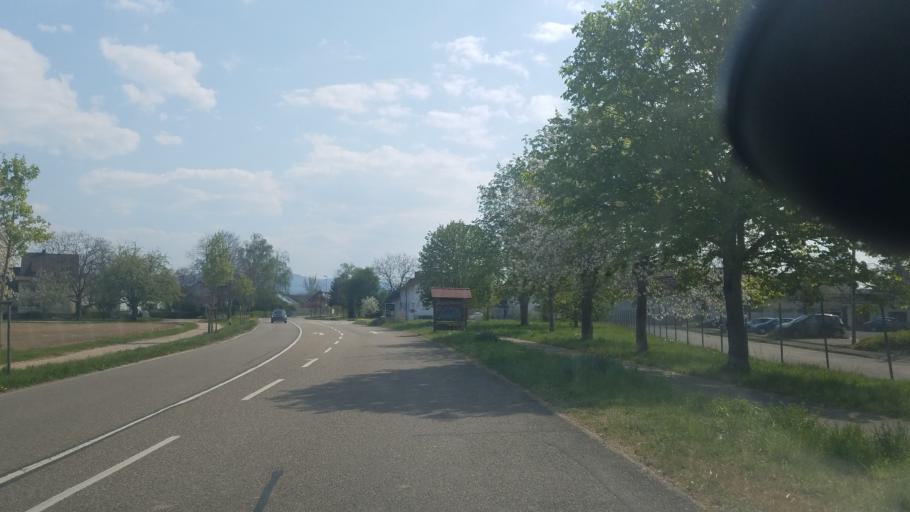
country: DE
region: Baden-Wuerttemberg
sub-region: Freiburg Region
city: Achern
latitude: 48.6354
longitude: 8.0427
